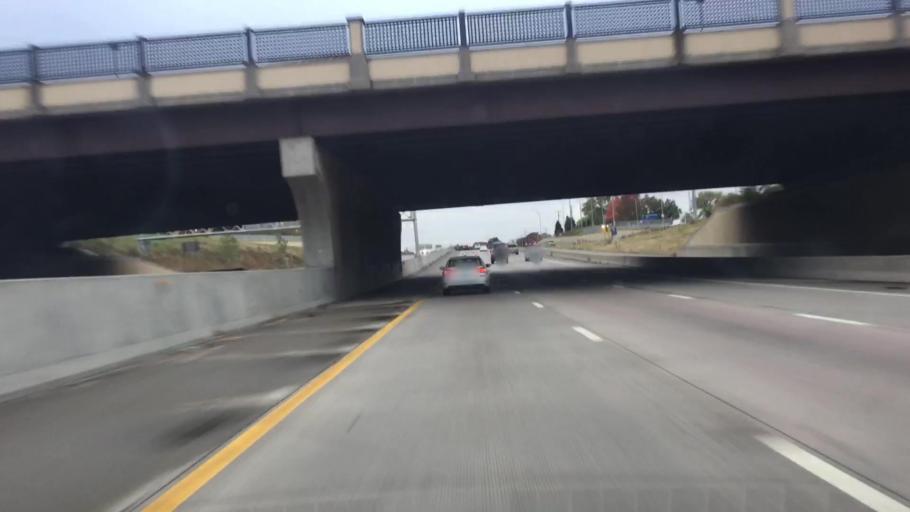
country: US
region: Kansas
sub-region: Johnson County
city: Lenexa
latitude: 38.9713
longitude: -94.7172
